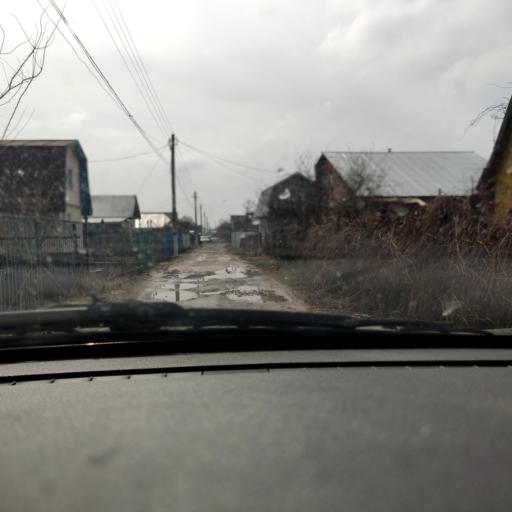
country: RU
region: Samara
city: Tol'yatti
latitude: 53.5860
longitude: 49.2914
